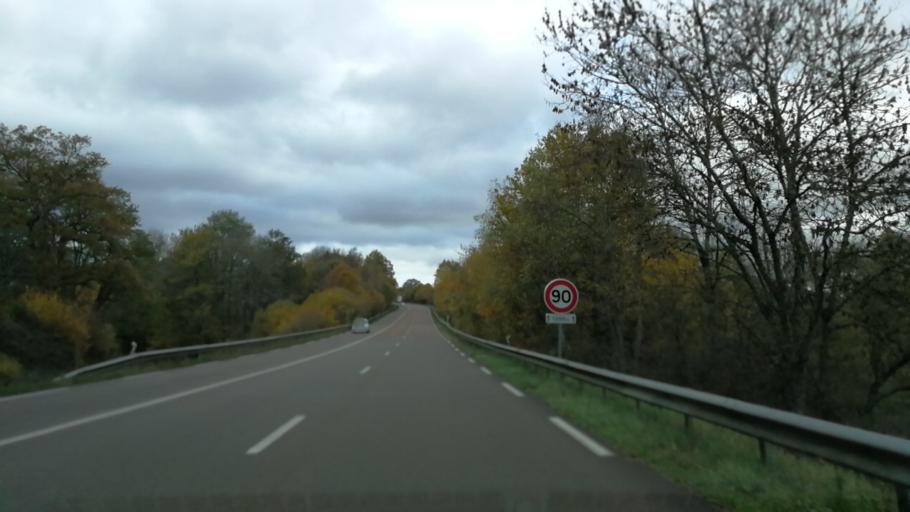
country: FR
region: Bourgogne
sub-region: Departement de la Cote-d'Or
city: Saulieu
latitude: 47.2582
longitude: 4.2678
